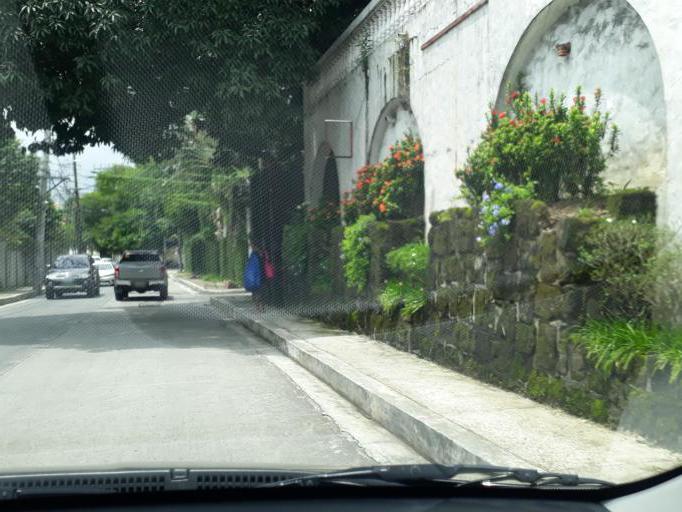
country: PH
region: Metro Manila
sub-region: San Juan
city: San Juan
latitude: 14.6216
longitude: 121.0391
